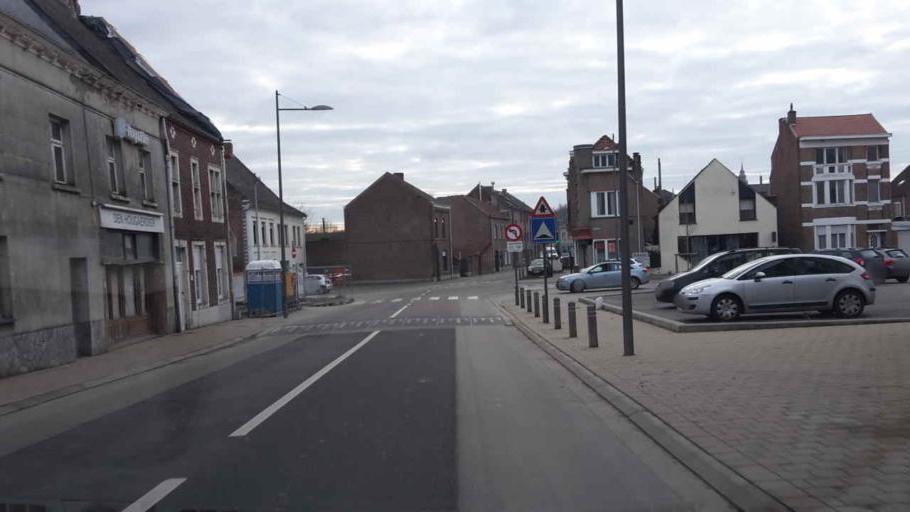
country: BE
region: Flanders
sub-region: Provincie Vlaams-Brabant
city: Hoegaarden
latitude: 50.7789
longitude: 4.8947
